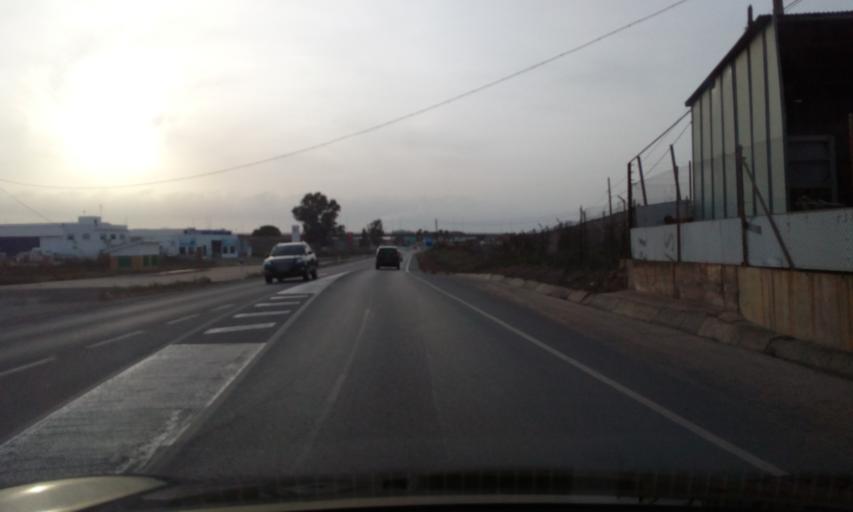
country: ES
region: Andalusia
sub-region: Provincia de Huelva
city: San Juan del Puerto
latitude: 37.3171
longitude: -6.8238
